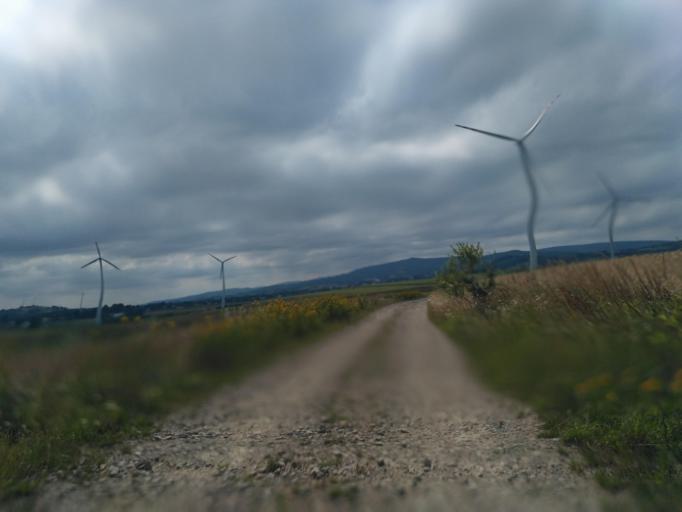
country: PL
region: Subcarpathian Voivodeship
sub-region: Powiat krosnienski
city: Rymanow
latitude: 49.6038
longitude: 21.8474
